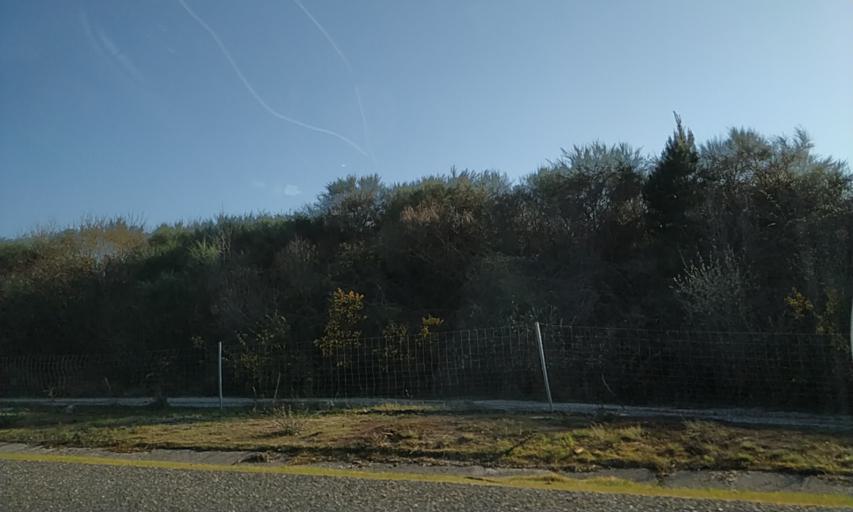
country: ES
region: Galicia
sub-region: Provincia de Lugo
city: Lugo
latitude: 43.0497
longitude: -7.5482
